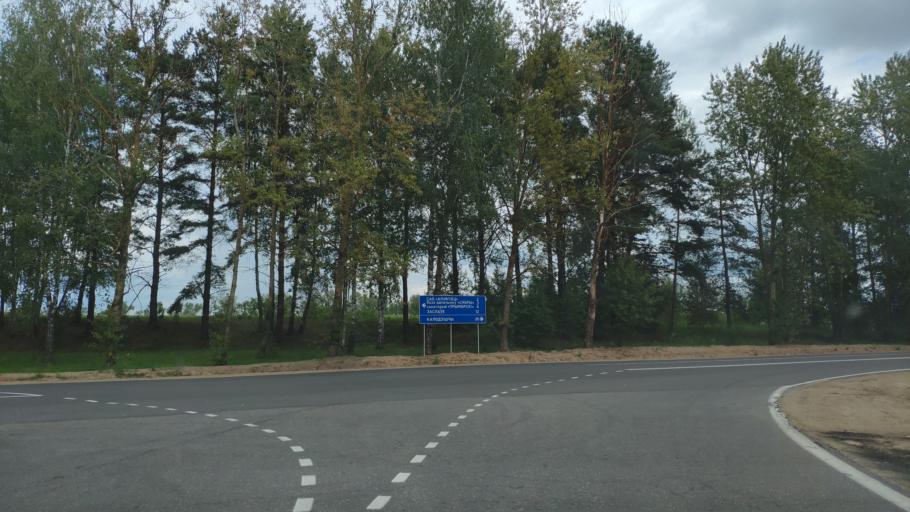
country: BY
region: Minsk
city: Syomkava
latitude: 53.9932
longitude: 27.4697
